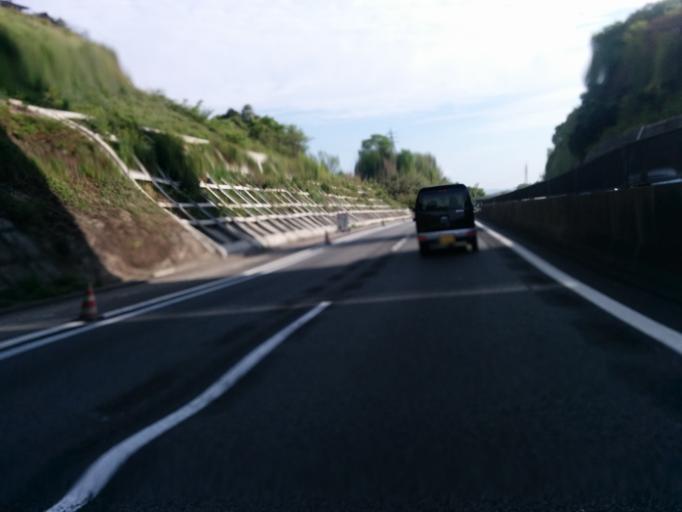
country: JP
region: Mie
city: Komono
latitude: 34.9779
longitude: 136.5141
